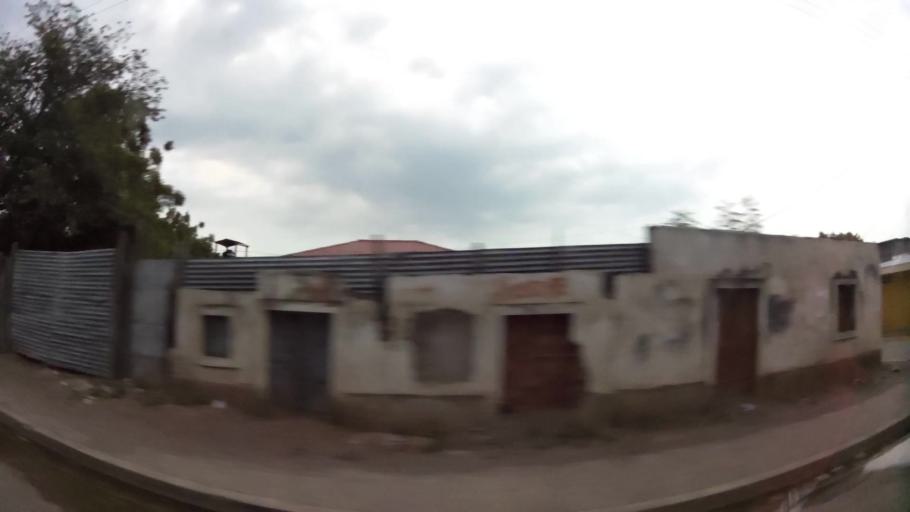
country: NI
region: Matagalpa
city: Ciudad Dario
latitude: 12.8501
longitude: -86.0951
